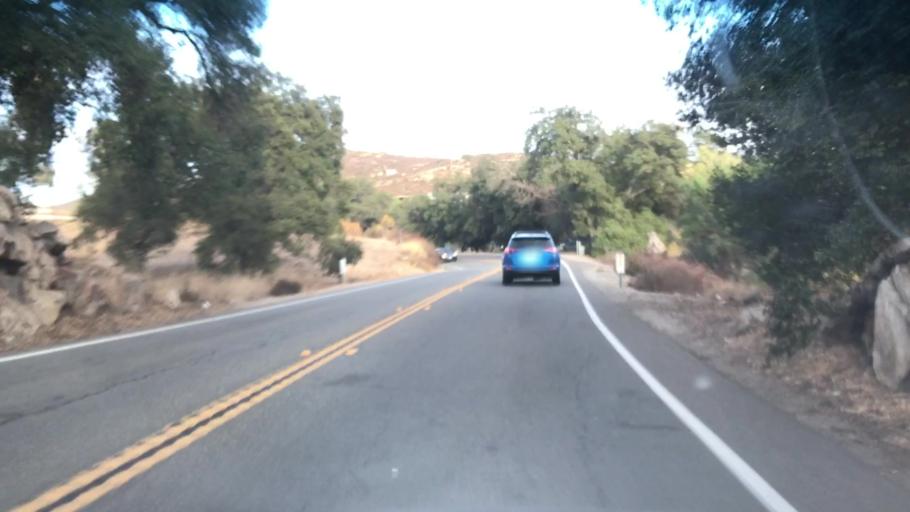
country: US
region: California
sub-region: San Diego County
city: Ramona
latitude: 33.0595
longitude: -116.8155
